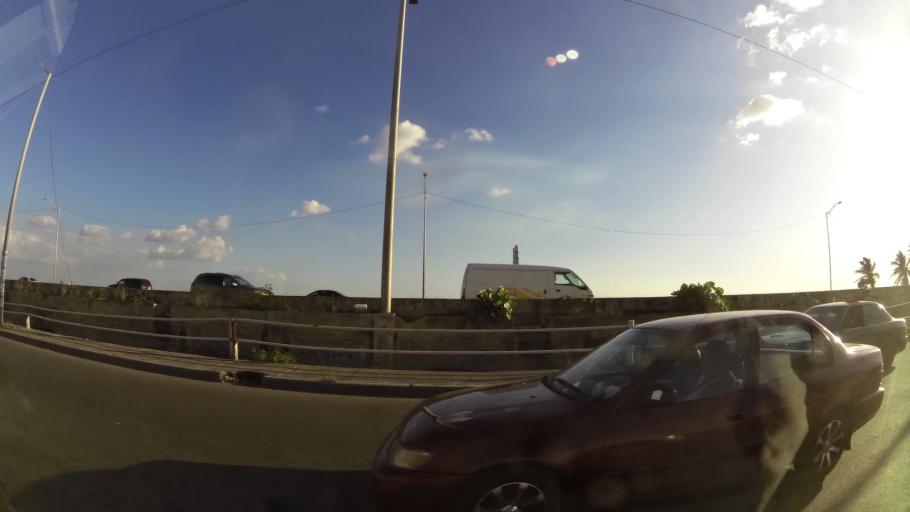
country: DO
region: Santo Domingo
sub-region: Santo Domingo
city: Santo Domingo Este
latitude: 18.4653
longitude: -69.8182
